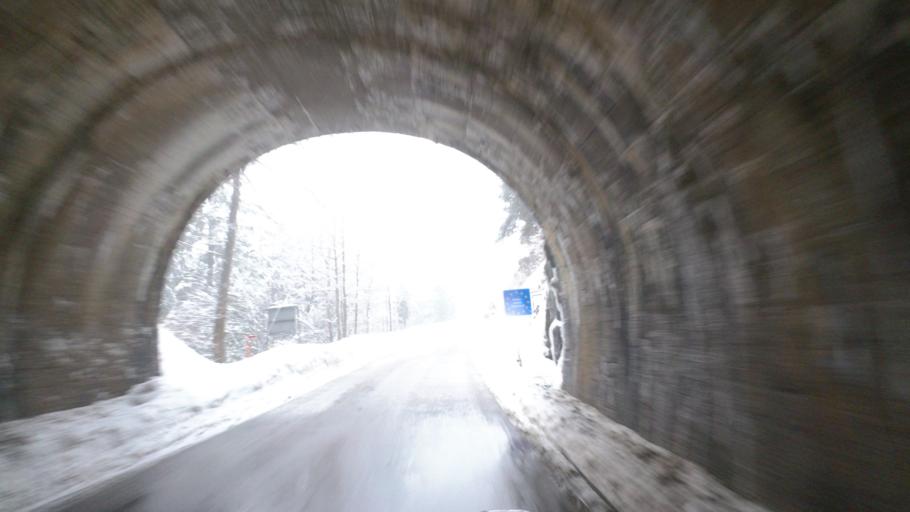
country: AT
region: Tyrol
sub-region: Politischer Bezirk Kitzbuhel
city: Kossen
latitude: 47.6902
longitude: 12.3951
